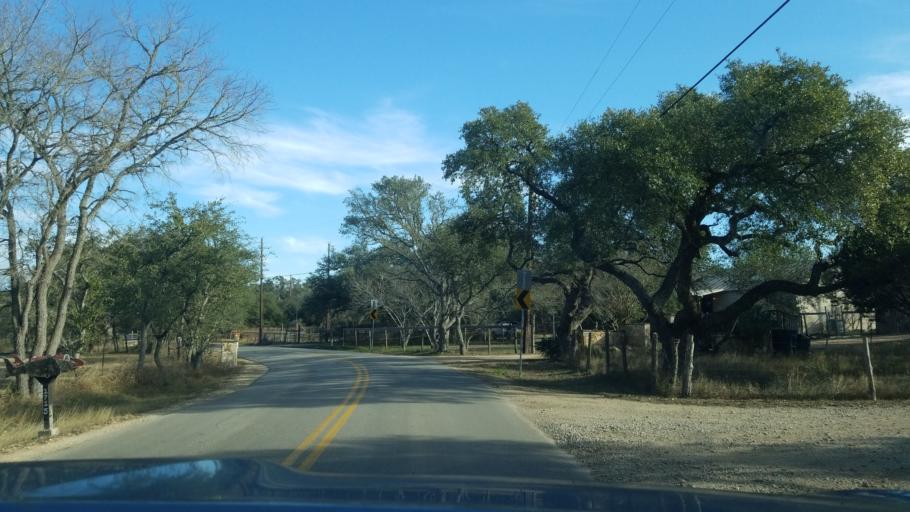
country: US
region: Texas
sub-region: Comal County
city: Canyon Lake
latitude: 29.7802
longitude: -98.2793
